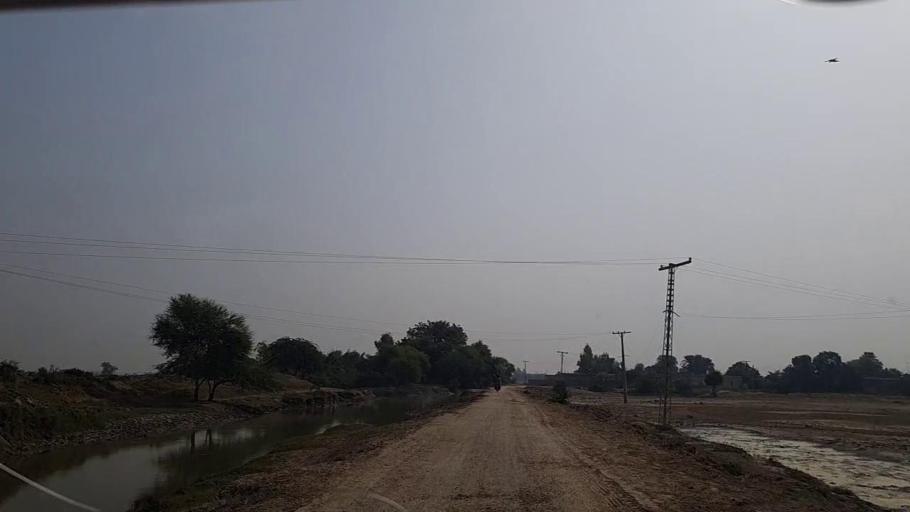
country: PK
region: Sindh
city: Garhi Yasin
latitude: 27.9237
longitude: 68.5688
